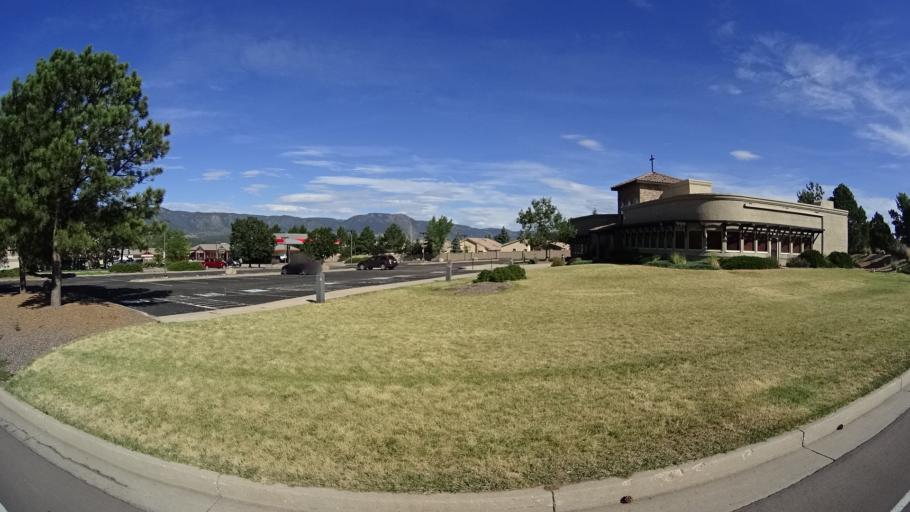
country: US
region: Colorado
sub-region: El Paso County
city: Gleneagle
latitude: 39.0331
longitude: -104.8286
